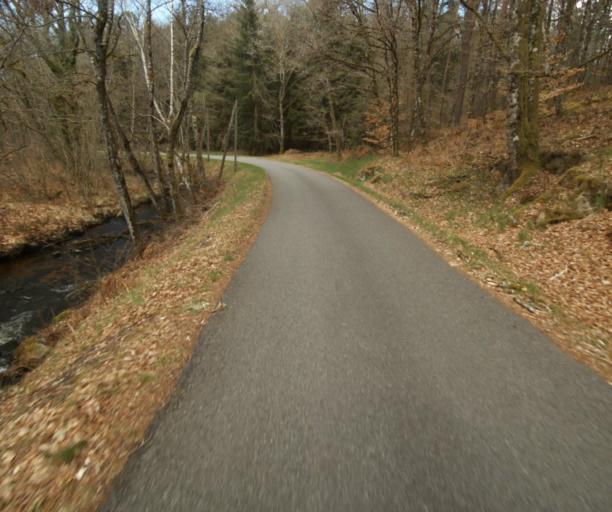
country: FR
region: Limousin
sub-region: Departement de la Correze
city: Laguenne
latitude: 45.2309
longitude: 1.9060
